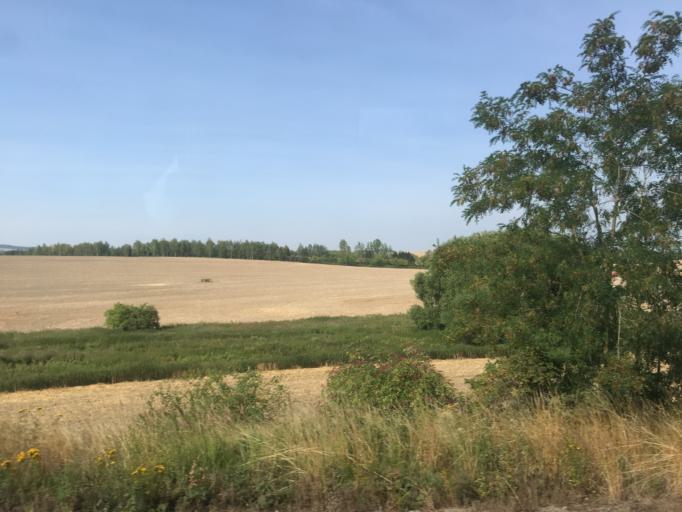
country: CZ
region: Central Bohemia
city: Bystrice
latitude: 49.7514
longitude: 14.6782
